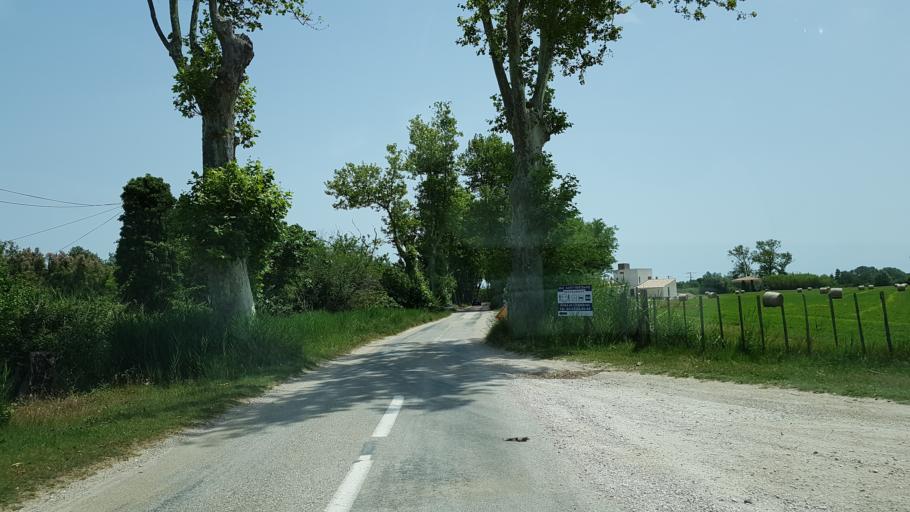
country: FR
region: Provence-Alpes-Cote d'Azur
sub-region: Departement des Bouches-du-Rhone
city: Port-Saint-Louis-du-Rhone
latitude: 43.4497
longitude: 4.6603
